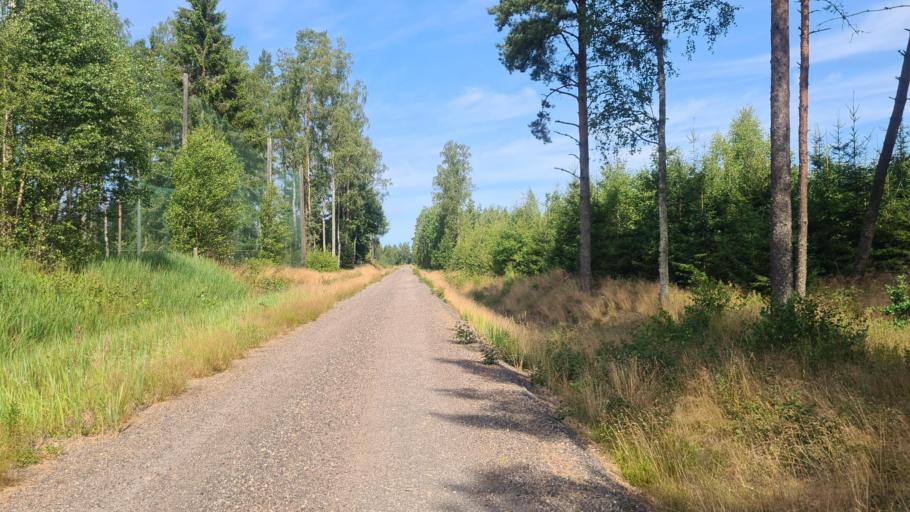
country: SE
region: Kronoberg
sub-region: Ljungby Kommun
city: Lagan
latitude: 56.9241
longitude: 13.9854
